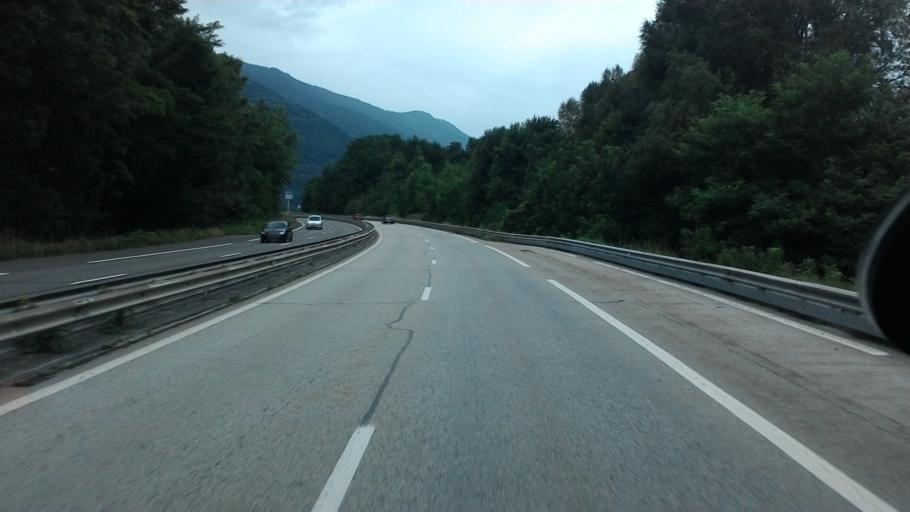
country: FR
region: Rhone-Alpes
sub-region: Departement de la Savoie
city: La Bathie
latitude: 45.5815
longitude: 6.4587
